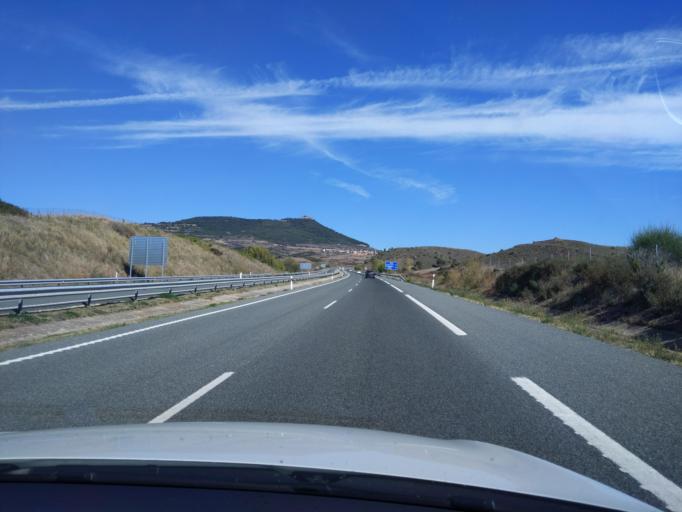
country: ES
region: Navarre
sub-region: Provincia de Navarra
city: Villamayor de Monjardin
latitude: 42.6076
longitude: -2.1138
